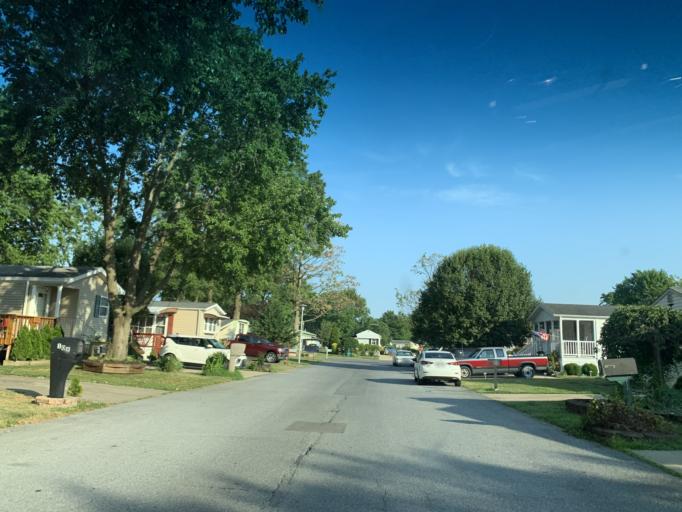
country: US
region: Maryland
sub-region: Baltimore County
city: Bowleys Quarters
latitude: 39.3397
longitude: -76.4048
